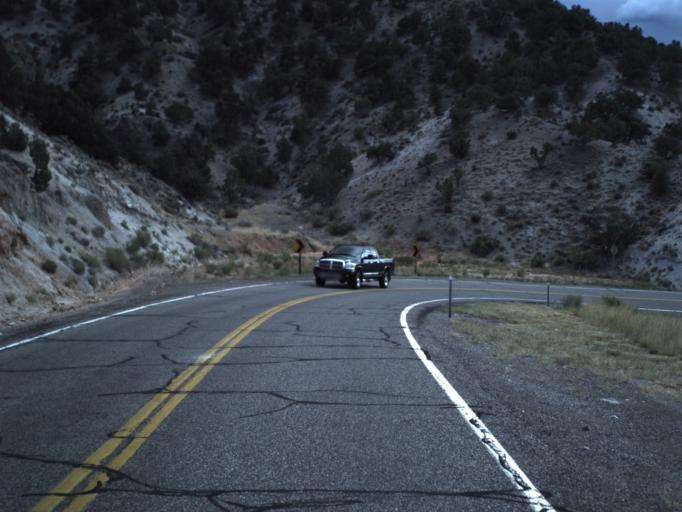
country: US
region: Utah
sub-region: Sevier County
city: Richfield
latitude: 38.7747
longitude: -111.9460
